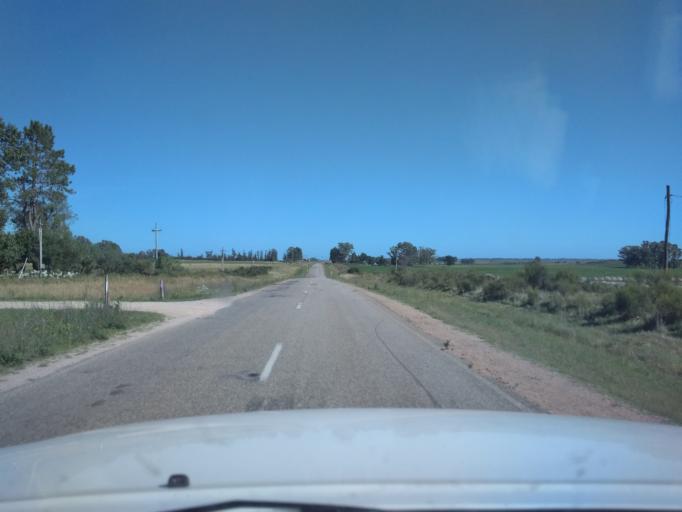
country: UY
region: Canelones
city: San Ramon
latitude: -34.1985
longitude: -55.9353
